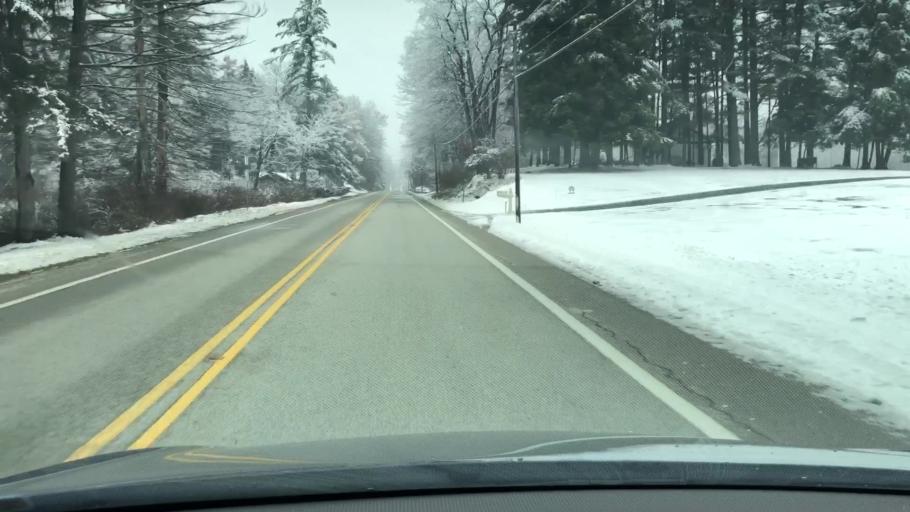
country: US
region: Pennsylvania
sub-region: Fayette County
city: Hopwood
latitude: 39.8292
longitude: -79.5981
